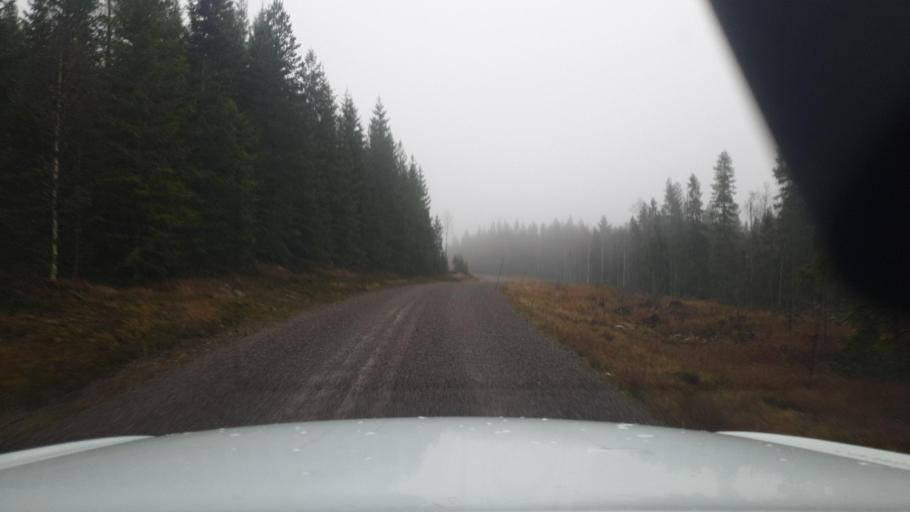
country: SE
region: Vaermland
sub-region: Eda Kommun
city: Charlottenberg
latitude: 60.0764
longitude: 12.6205
